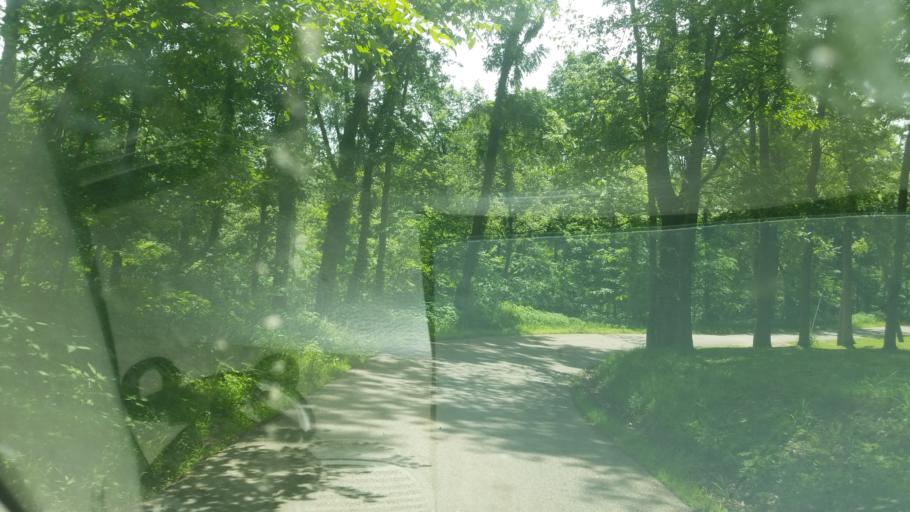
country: US
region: Ohio
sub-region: Sandusky County
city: Bellville
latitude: 40.6194
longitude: -82.4639
